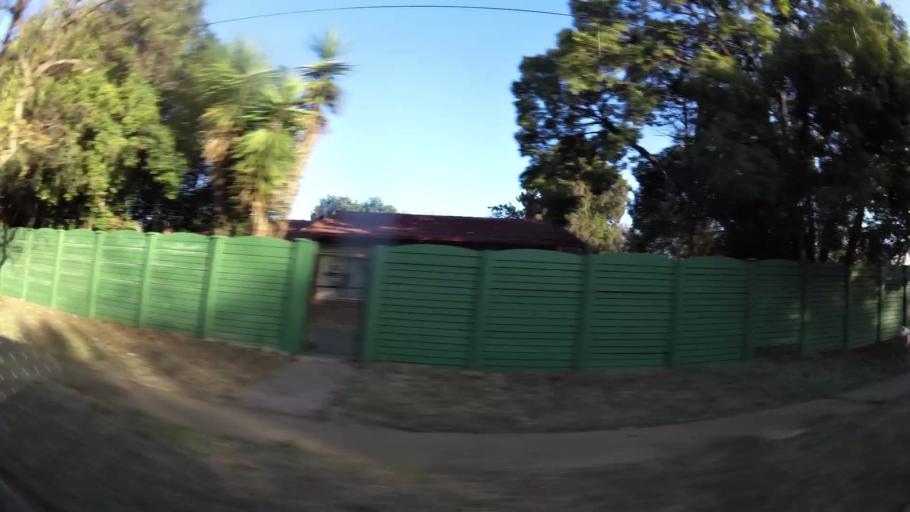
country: ZA
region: Gauteng
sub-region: City of Tshwane Metropolitan Municipality
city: Pretoria
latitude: -25.7151
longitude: 28.2255
